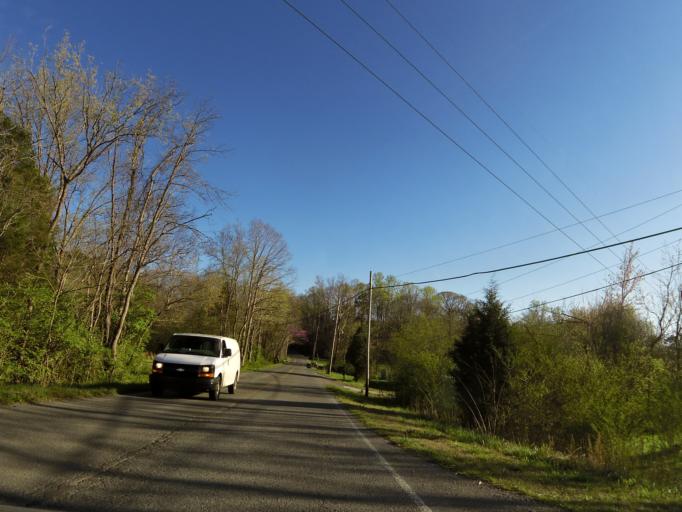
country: US
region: Tennessee
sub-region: Knox County
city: Mascot
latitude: 36.0030
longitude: -83.7665
